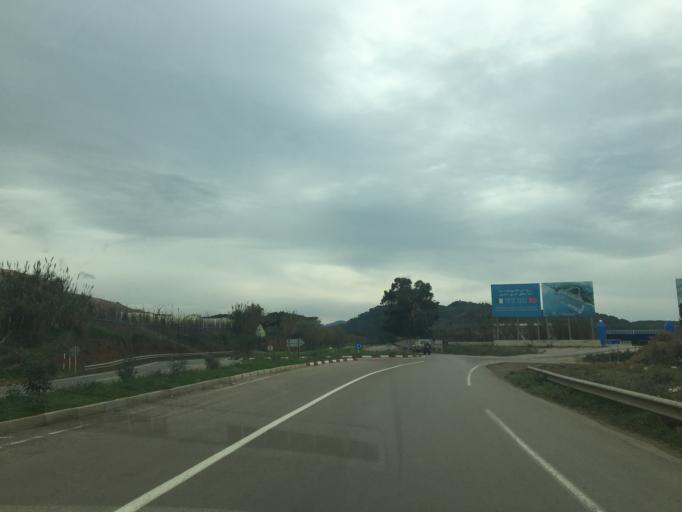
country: DZ
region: Tipaza
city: Hadjout
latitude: 36.6229
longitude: 2.2639
